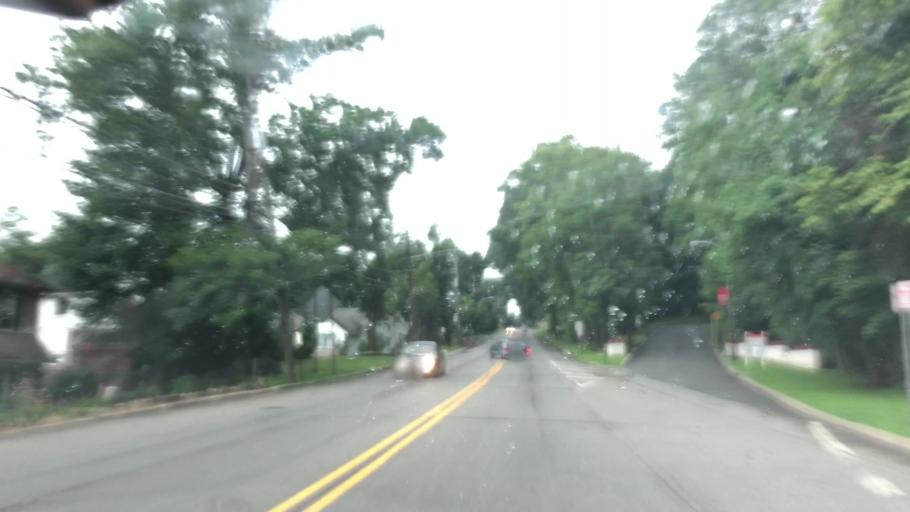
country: US
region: New Jersey
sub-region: Passaic County
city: Little Falls
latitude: 40.8672
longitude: -74.1917
